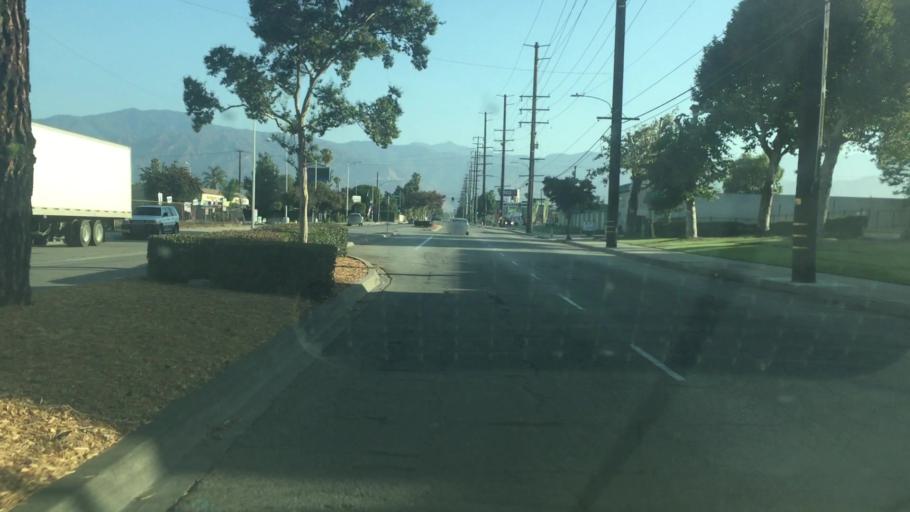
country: US
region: California
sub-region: Los Angeles County
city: Irwindale
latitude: 34.0875
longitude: -117.9254
